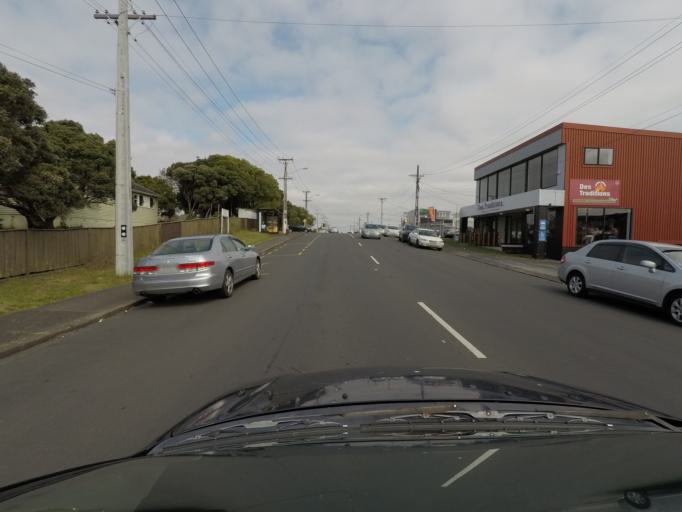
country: NZ
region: Auckland
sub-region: Auckland
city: Auckland
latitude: -36.9055
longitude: 174.7306
